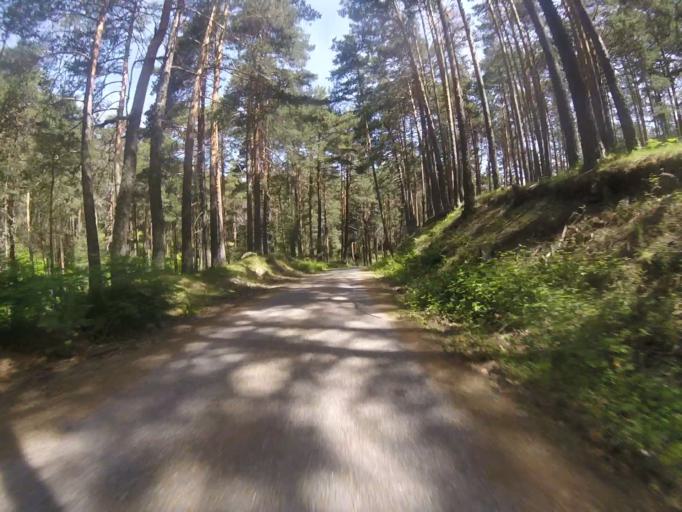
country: ES
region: Madrid
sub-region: Provincia de Madrid
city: Cercedilla
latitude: 40.8183
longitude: -4.0288
